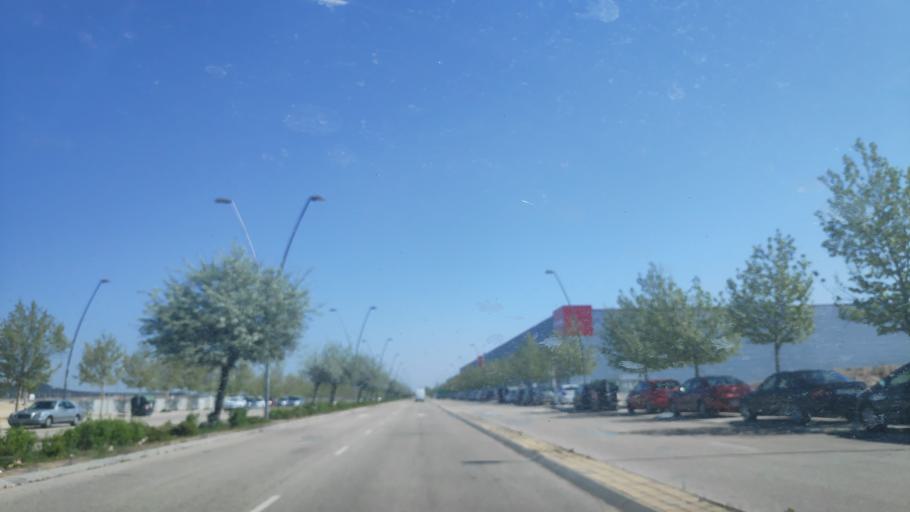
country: ES
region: Madrid
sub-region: Provincia de Madrid
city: Pinto
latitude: 40.2827
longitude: -3.6864
